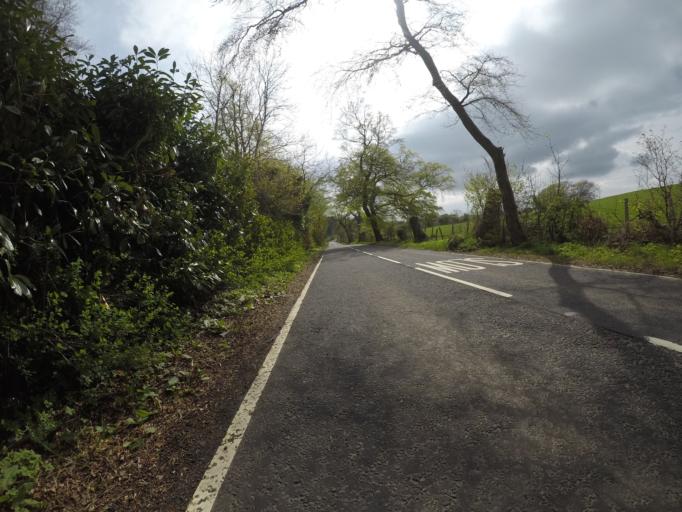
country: GB
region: Scotland
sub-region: East Renfrewshire
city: Newton Mearns
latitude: 55.7559
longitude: -4.3421
